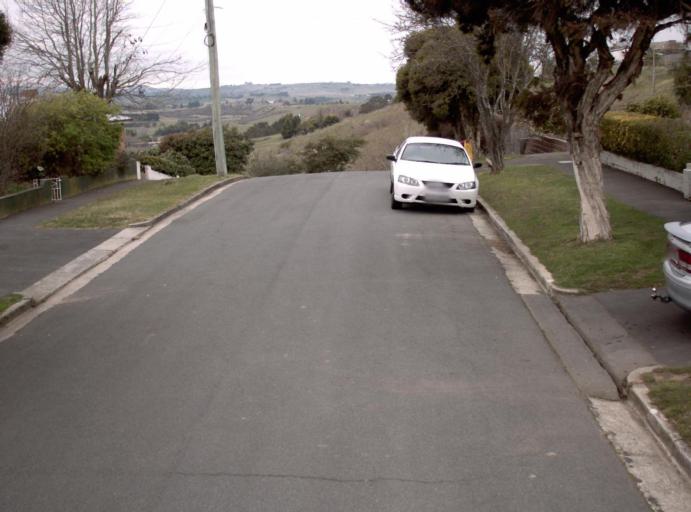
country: AU
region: Tasmania
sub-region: Launceston
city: Newstead
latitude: -41.4559
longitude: 147.1795
